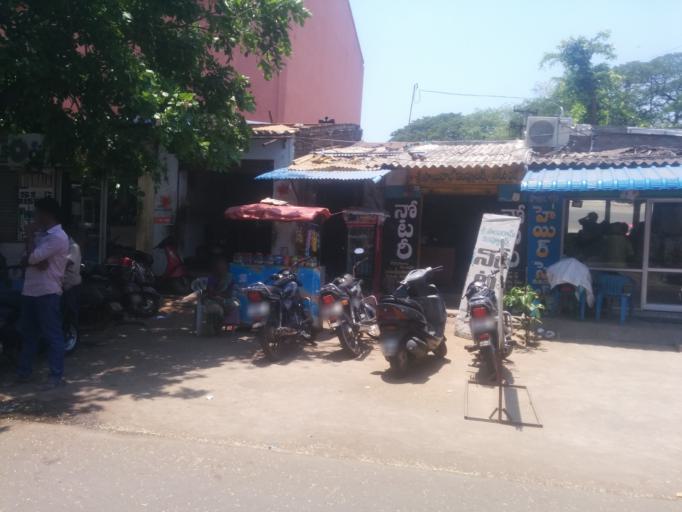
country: IN
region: Andhra Pradesh
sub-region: East Godavari
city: Rajahmundry
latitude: 17.0104
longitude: 81.7709
